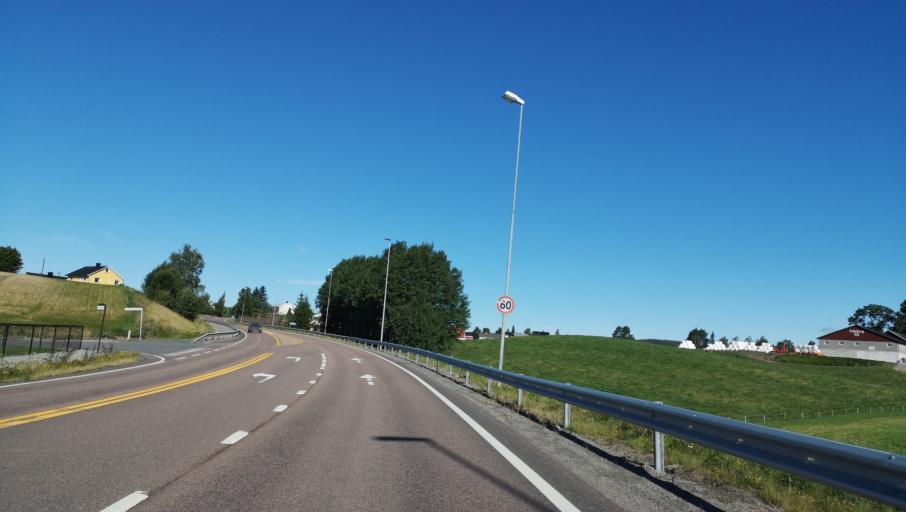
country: NO
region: Ostfold
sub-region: Spydeberg
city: Spydeberg
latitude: 59.6105
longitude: 11.0942
